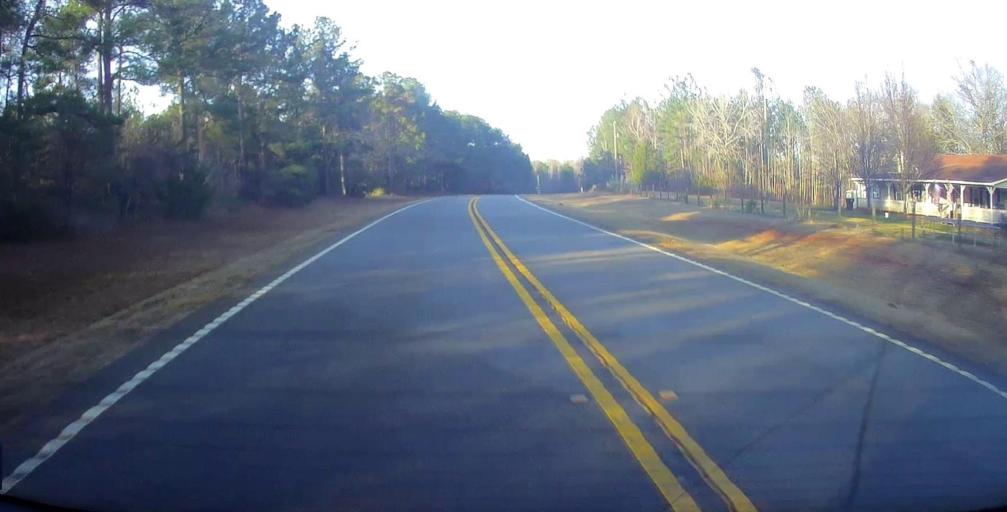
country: US
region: Georgia
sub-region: Upson County
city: Thomaston
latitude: 32.8525
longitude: -84.4199
